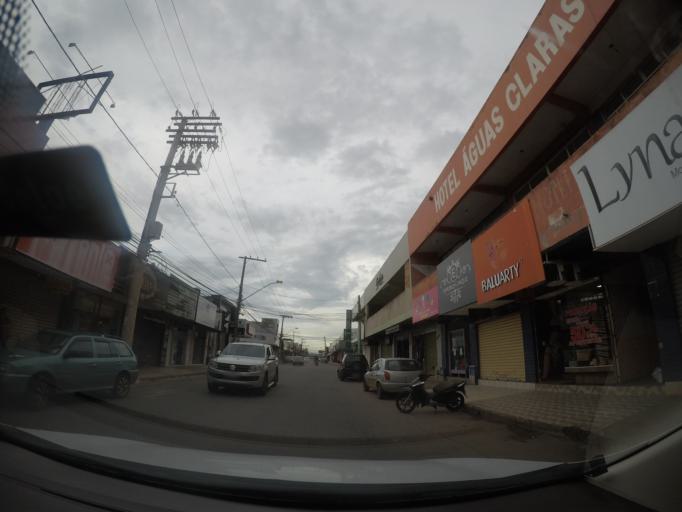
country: BR
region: Goias
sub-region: Goiania
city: Goiania
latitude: -16.6615
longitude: -49.2758
